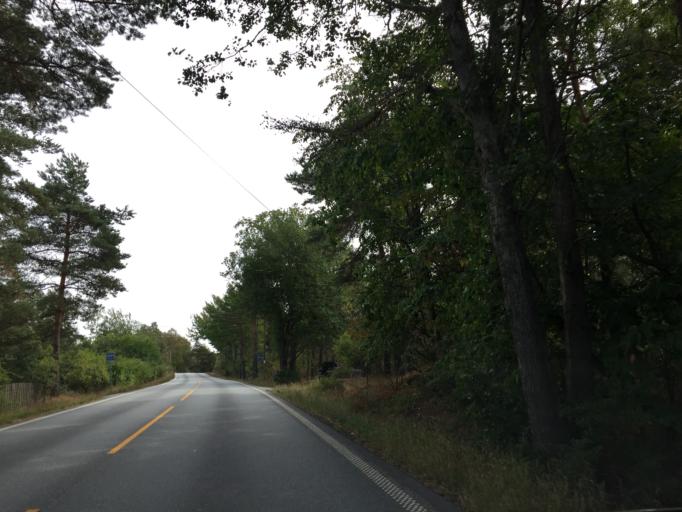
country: NO
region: Ostfold
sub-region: Hvaler
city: Skjaerhalden
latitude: 59.0664
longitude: 10.9357
